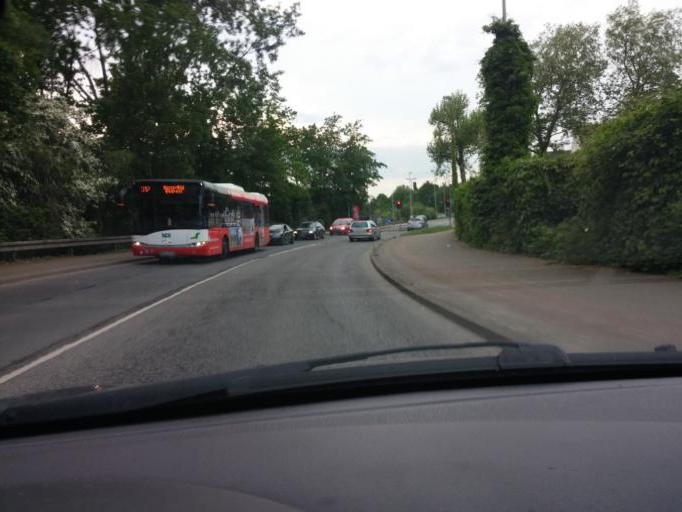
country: DE
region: North Rhine-Westphalia
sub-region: Regierungsbezirk Munster
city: Gelsenkirchen
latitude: 51.5463
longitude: 7.1418
